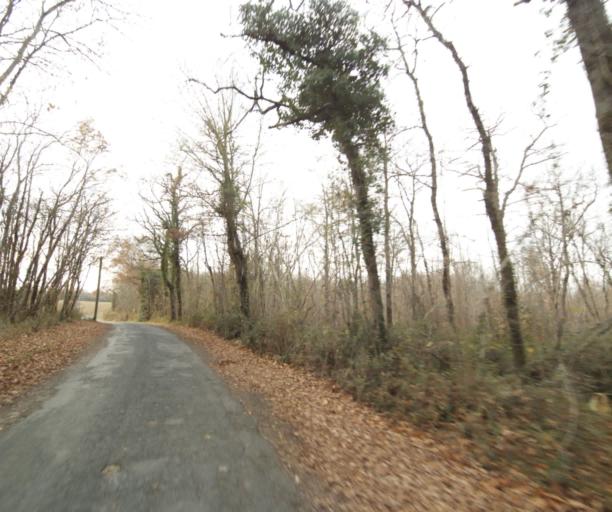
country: FR
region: Poitou-Charentes
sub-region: Departement de la Charente-Maritime
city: Fontcouverte
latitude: 45.7886
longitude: -0.5904
